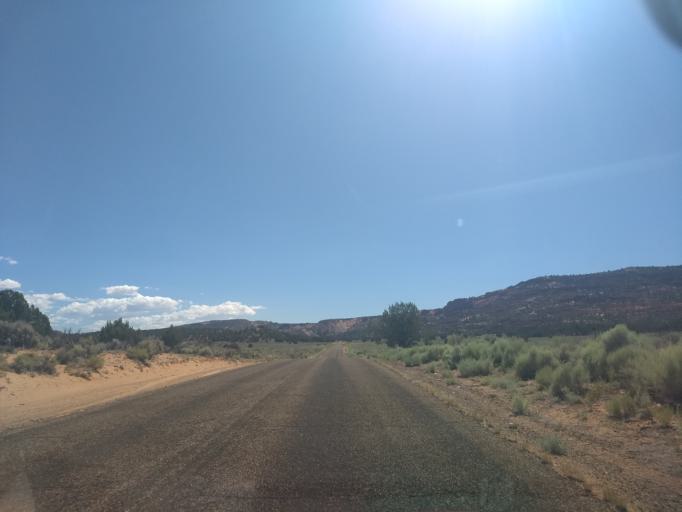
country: US
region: Utah
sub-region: Washington County
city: Hildale
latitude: 37.0131
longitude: -112.8441
